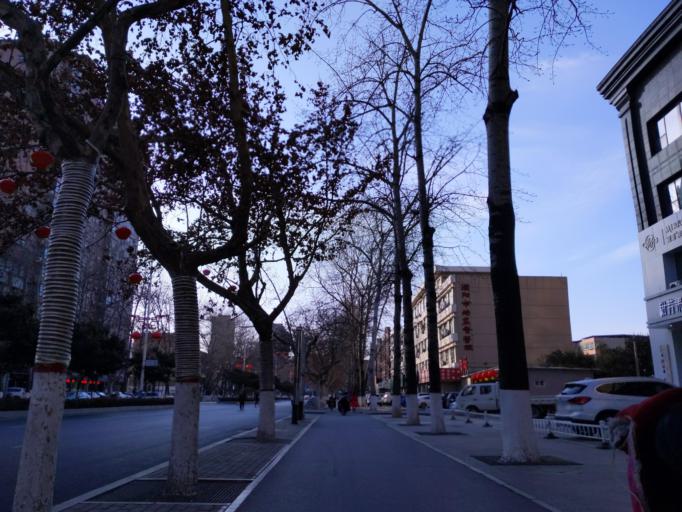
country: CN
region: Henan Sheng
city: Puyang
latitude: 35.7619
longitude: 115.0170
